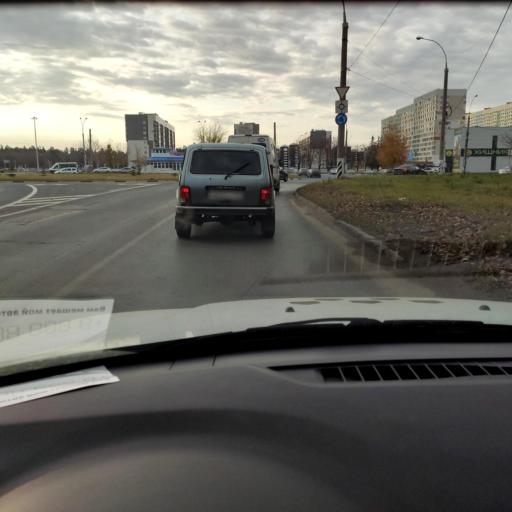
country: RU
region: Samara
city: Tol'yatti
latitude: 53.5331
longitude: 49.3433
